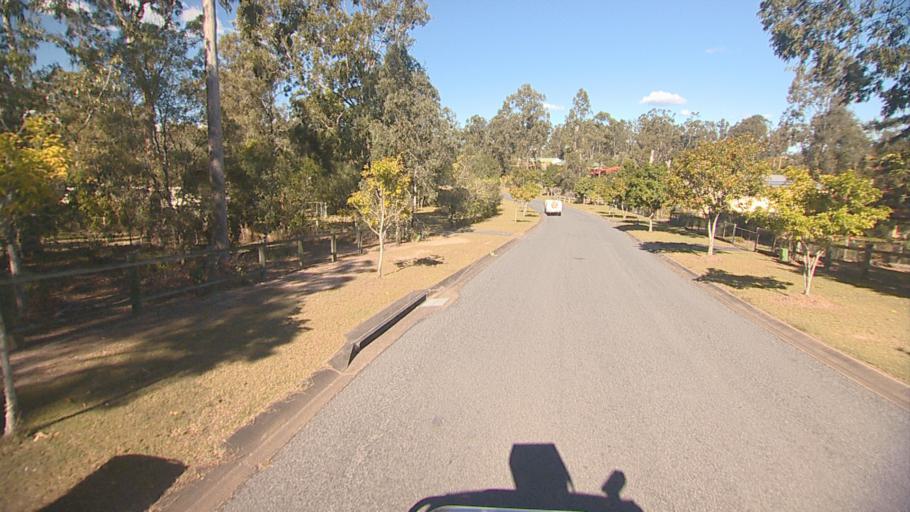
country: AU
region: Queensland
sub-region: Ipswich
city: Springfield Lakes
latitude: -27.7243
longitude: 152.9198
